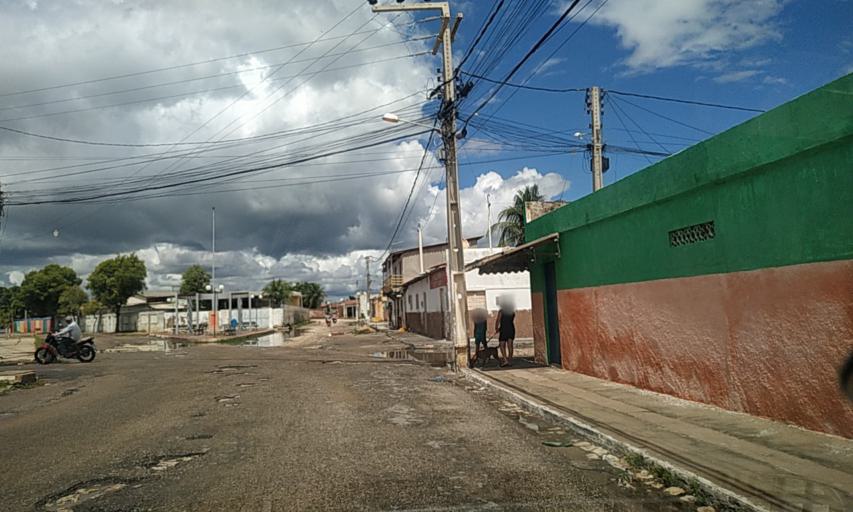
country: BR
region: Rio Grande do Norte
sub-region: Areia Branca
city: Areia Branca
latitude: -4.9535
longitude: -37.1277
